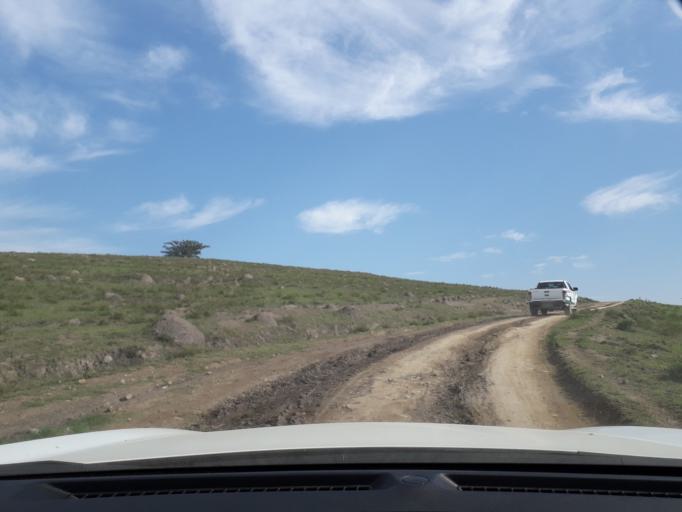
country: ZA
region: Eastern Cape
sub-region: Buffalo City Metropolitan Municipality
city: Bhisho
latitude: -33.0036
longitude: 27.3237
